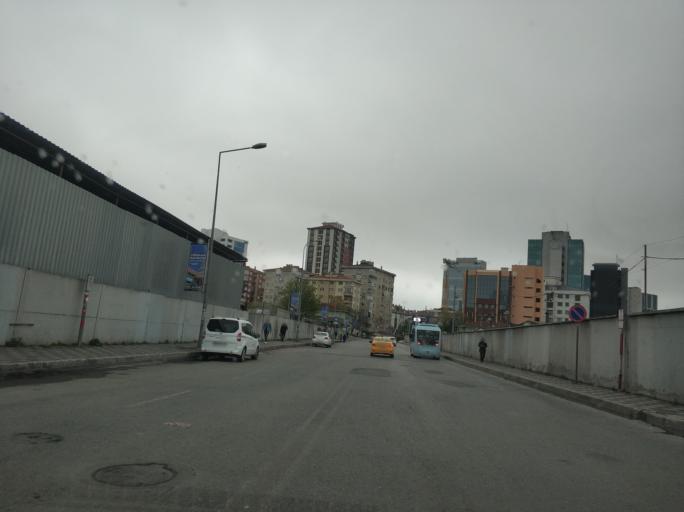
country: TR
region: Istanbul
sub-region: Atasehir
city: Atasehir
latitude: 40.9783
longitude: 29.1039
